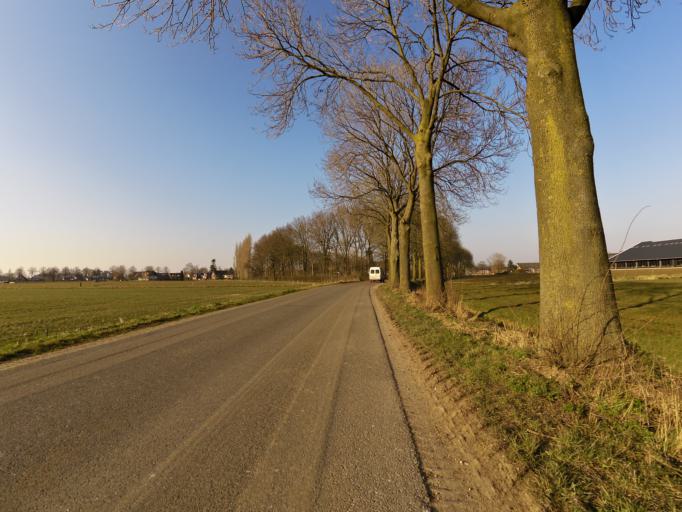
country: NL
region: Gelderland
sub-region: Gemeente Montferland
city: s-Heerenberg
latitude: 51.8826
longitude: 6.3044
